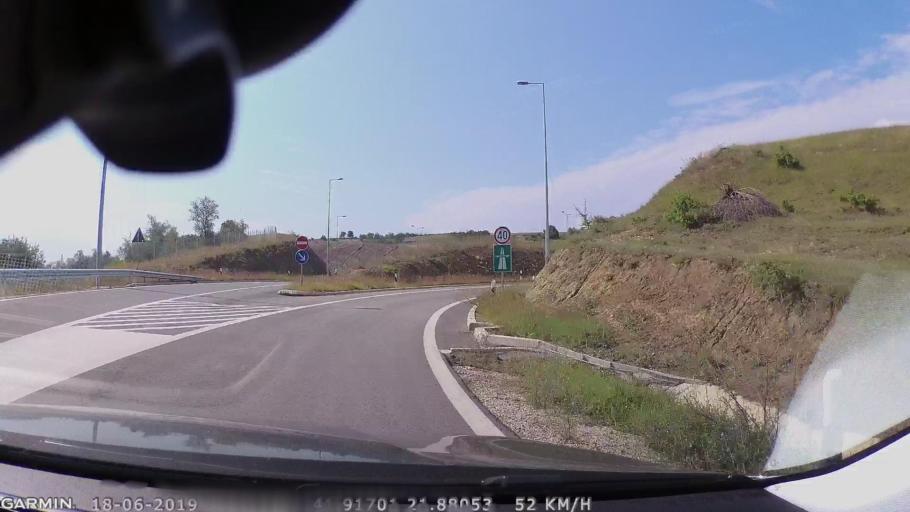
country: MK
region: Sveti Nikole
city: Gorobinci
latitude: 41.9167
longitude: 21.8807
